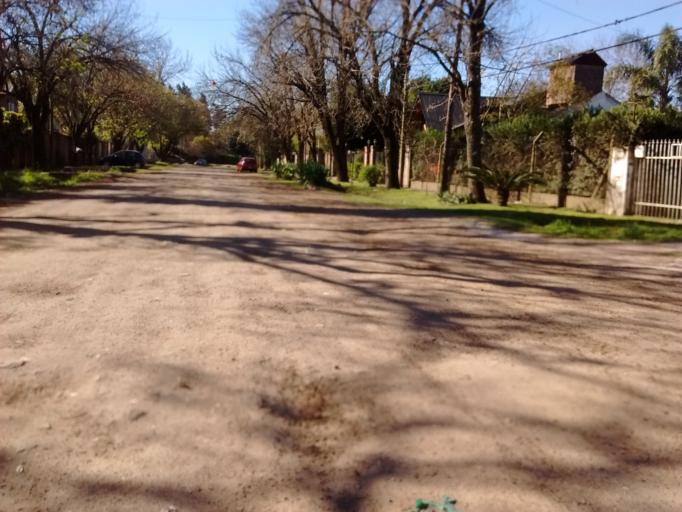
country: AR
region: Santa Fe
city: Funes
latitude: -32.9243
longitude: -60.8101
